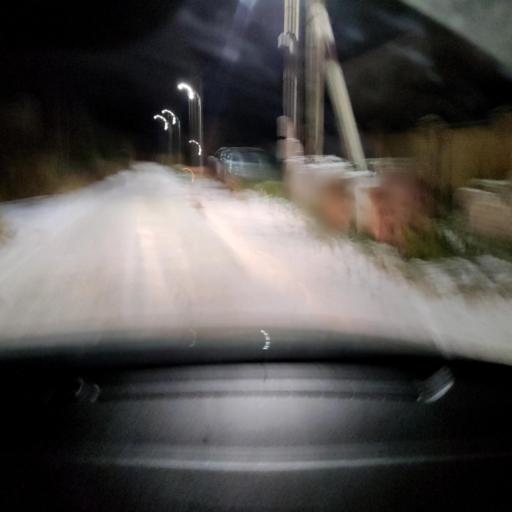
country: RU
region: Tatarstan
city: Stolbishchi
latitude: 55.7587
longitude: 49.2919
